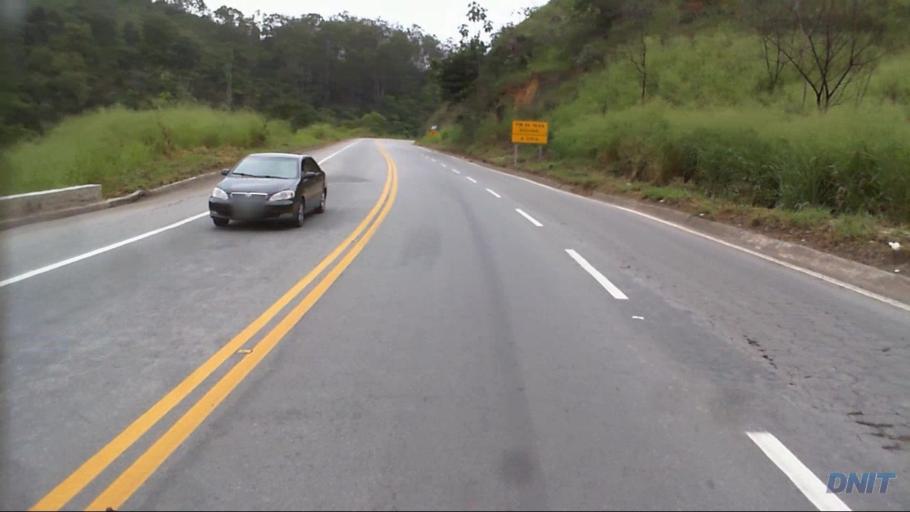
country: BR
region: Minas Gerais
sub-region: Timoteo
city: Timoteo
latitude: -19.6396
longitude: -42.8181
